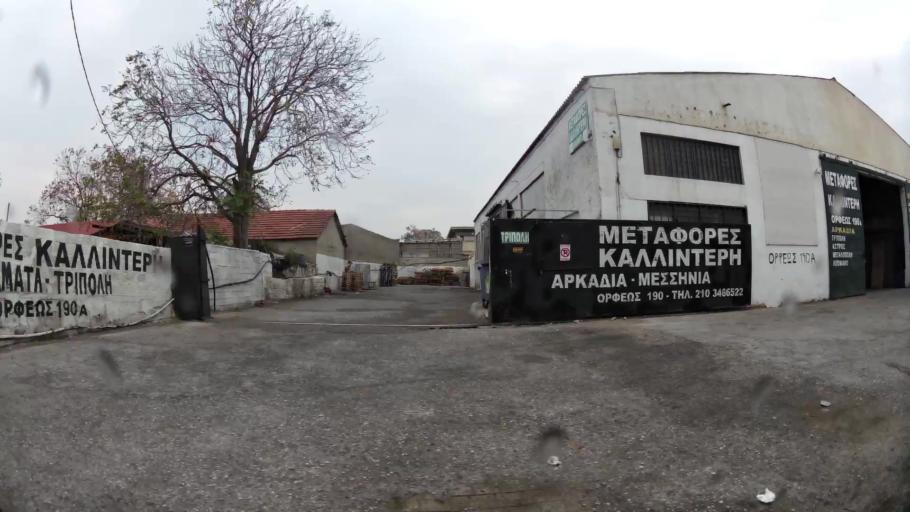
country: GR
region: Attica
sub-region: Nomarchia Athinas
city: Aigaleo
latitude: 37.9809
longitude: 23.6905
